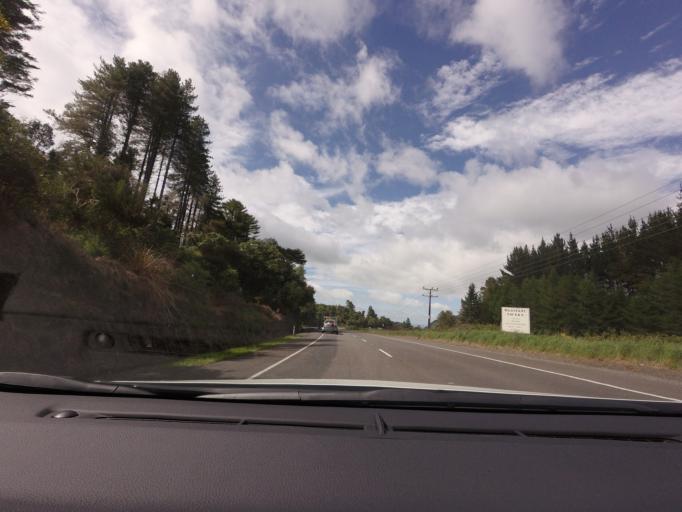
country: NZ
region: Bay of Plenty
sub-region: Rotorua District
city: Rotorua
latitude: -38.3270
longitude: 176.3692
